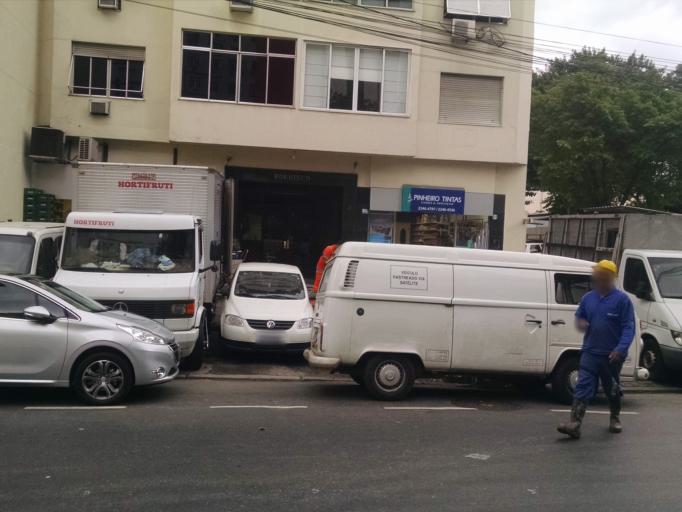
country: BR
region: Rio de Janeiro
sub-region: Rio De Janeiro
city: Rio de Janeiro
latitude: -22.9493
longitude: -43.1838
